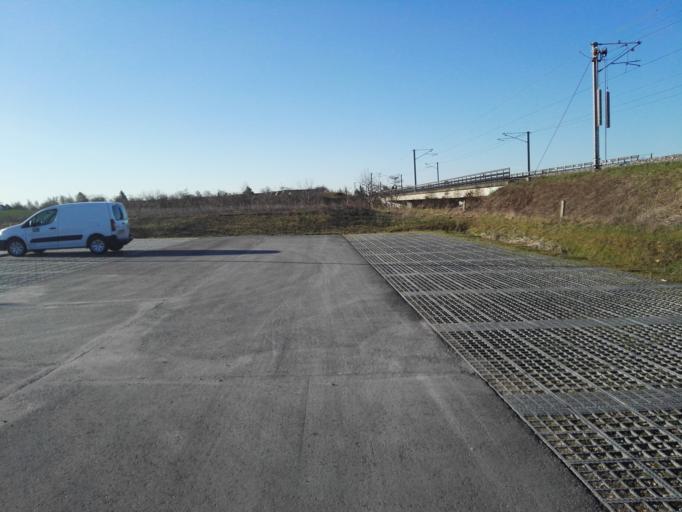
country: DK
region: Capital Region
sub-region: Egedal Kommune
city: Stenlose
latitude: 55.7775
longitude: 12.1867
